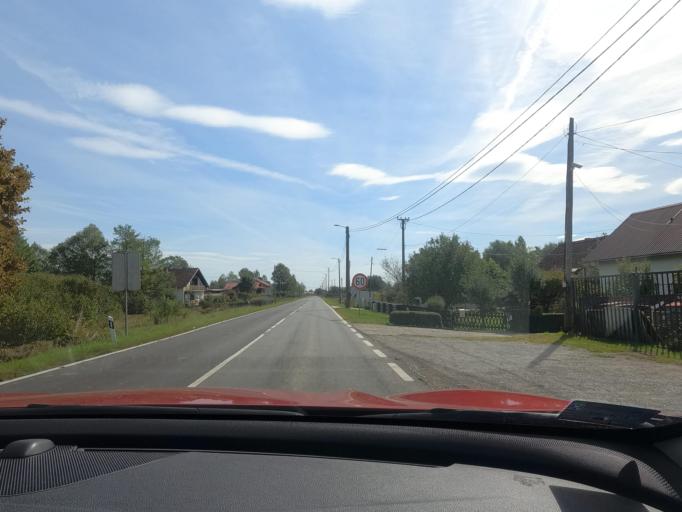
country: HR
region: Sisacko-Moslavacka
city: Budasevo
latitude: 45.4896
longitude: 16.4565
